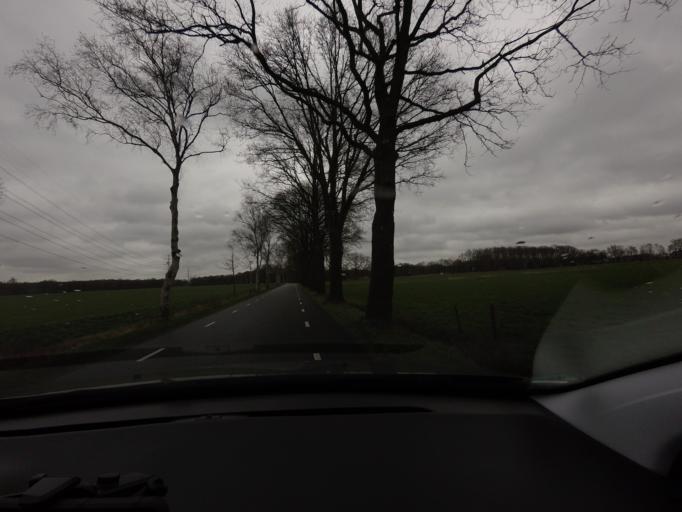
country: NL
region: Drenthe
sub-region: Gemeente Hoogeveen
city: Hoogeveen
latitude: 52.7600
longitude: 6.4897
